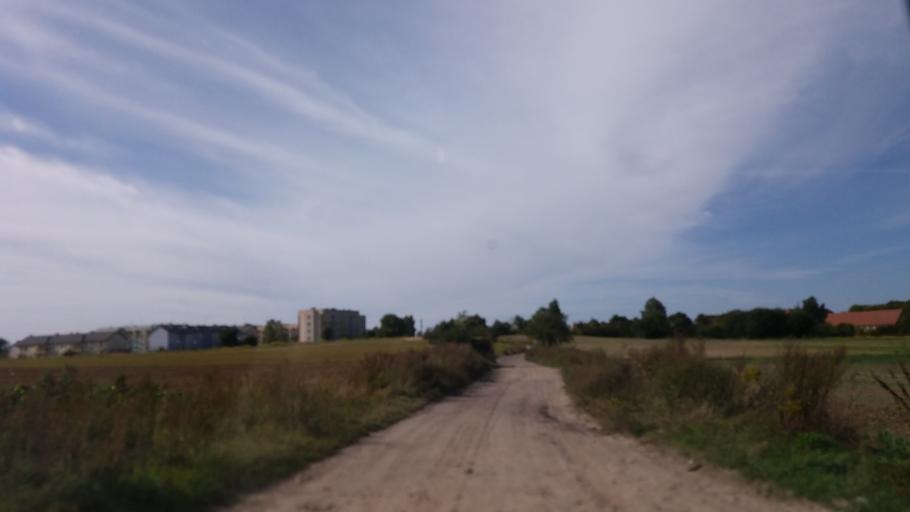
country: PL
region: West Pomeranian Voivodeship
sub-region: Powiat choszczenski
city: Choszczno
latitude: 53.1600
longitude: 15.4422
